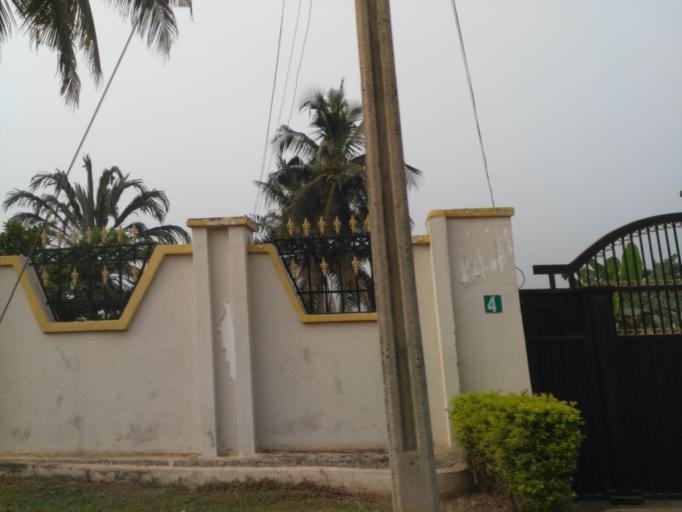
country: GH
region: Ashanti
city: Kumasi
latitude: 6.6531
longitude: -1.6205
